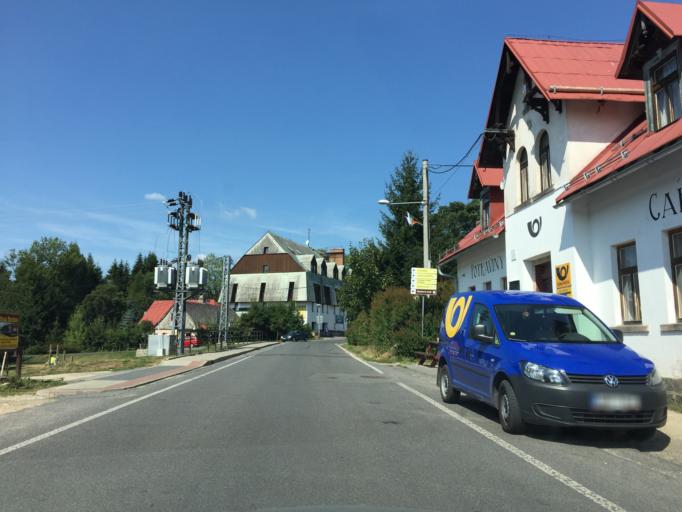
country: CZ
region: Liberecky
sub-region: Okres Jablonec nad Nisou
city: Janov nad Nisou
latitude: 50.7909
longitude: 15.1436
